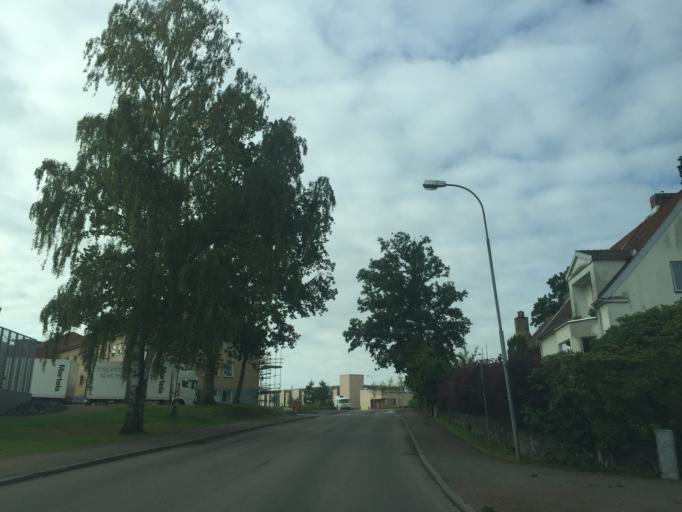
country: SE
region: Skane
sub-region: Angelholms Kommun
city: AEngelholm
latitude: 56.2407
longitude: 12.8576
